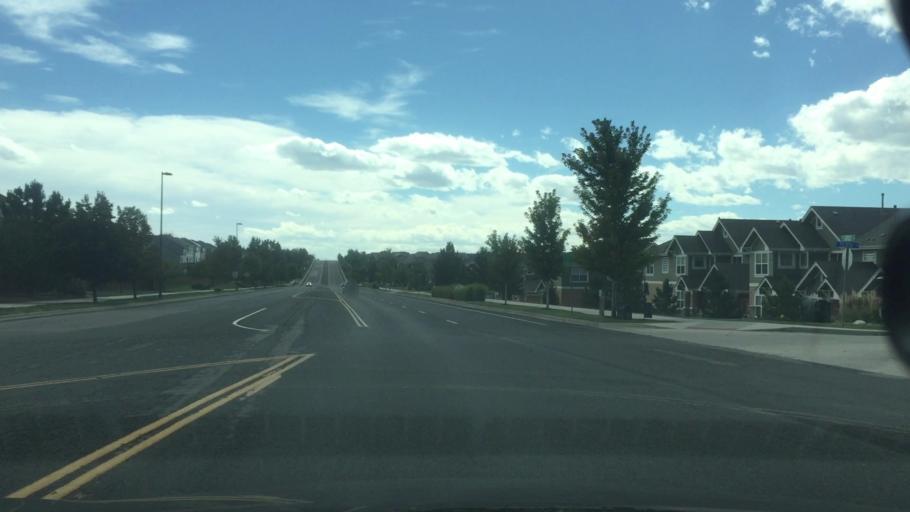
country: US
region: Colorado
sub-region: Arapahoe County
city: Dove Valley
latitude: 39.6496
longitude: -104.7351
